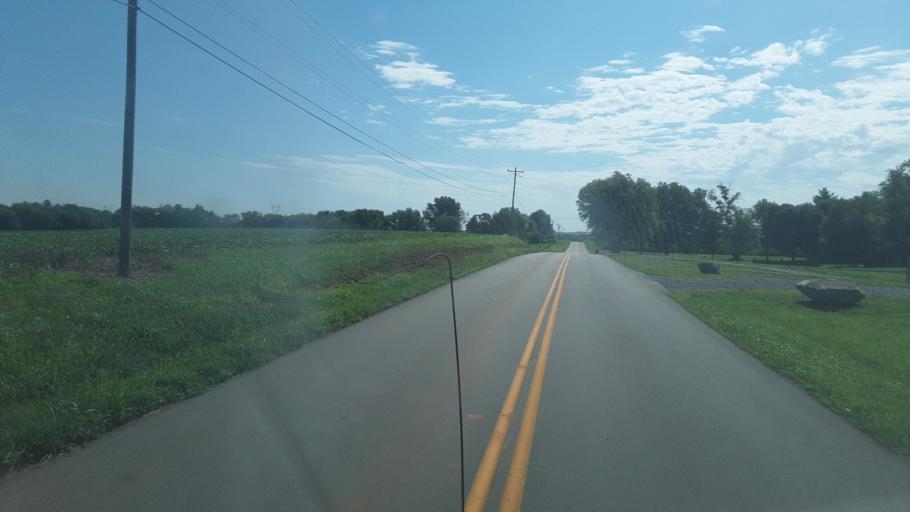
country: US
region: Kentucky
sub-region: Todd County
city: Elkton
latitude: 36.7390
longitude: -87.2410
